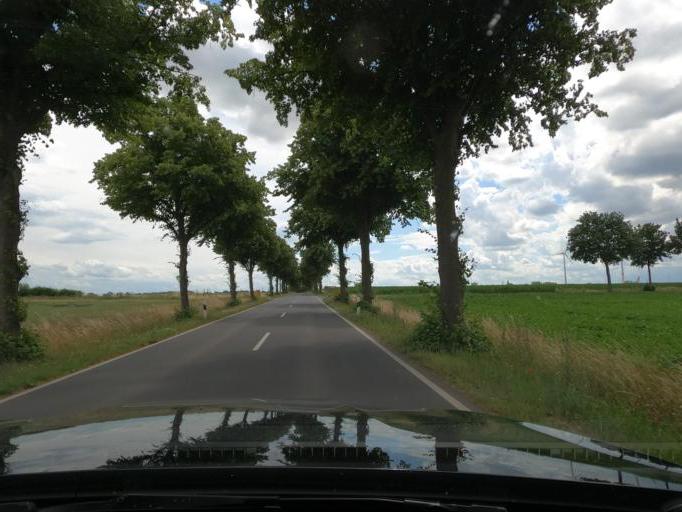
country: DE
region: Lower Saxony
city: Algermissen
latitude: 52.2640
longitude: 10.0130
